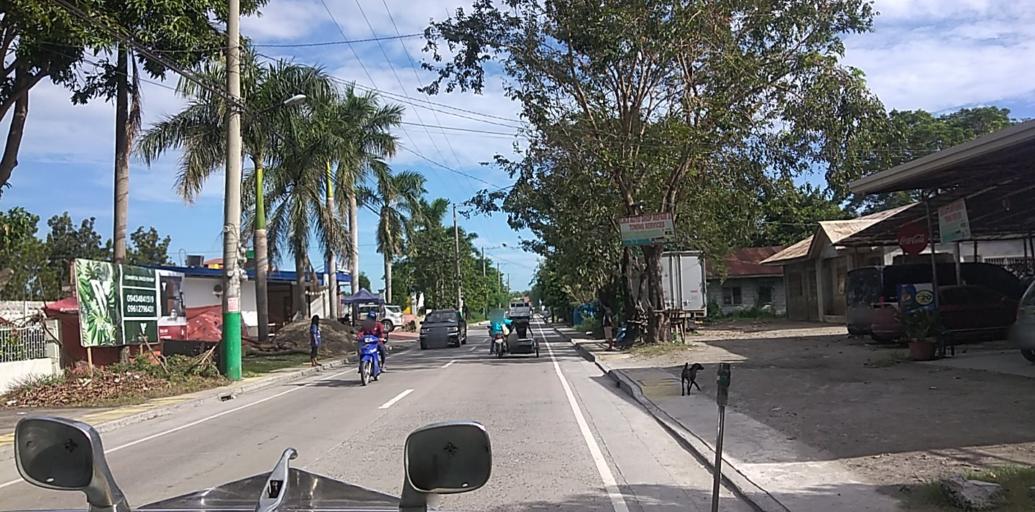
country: PH
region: Central Luzon
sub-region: Province of Pampanga
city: Malino
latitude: 15.1126
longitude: 120.6633
